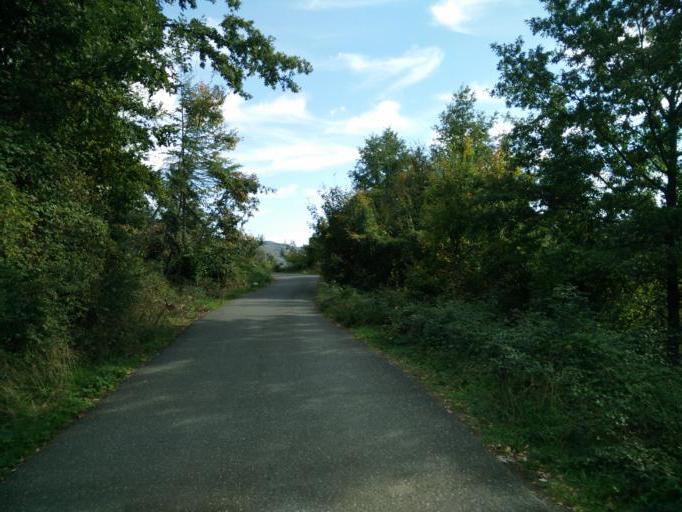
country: IT
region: Tuscany
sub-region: Provincia di Massa-Carrara
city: Patigno
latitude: 44.3541
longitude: 9.7514
